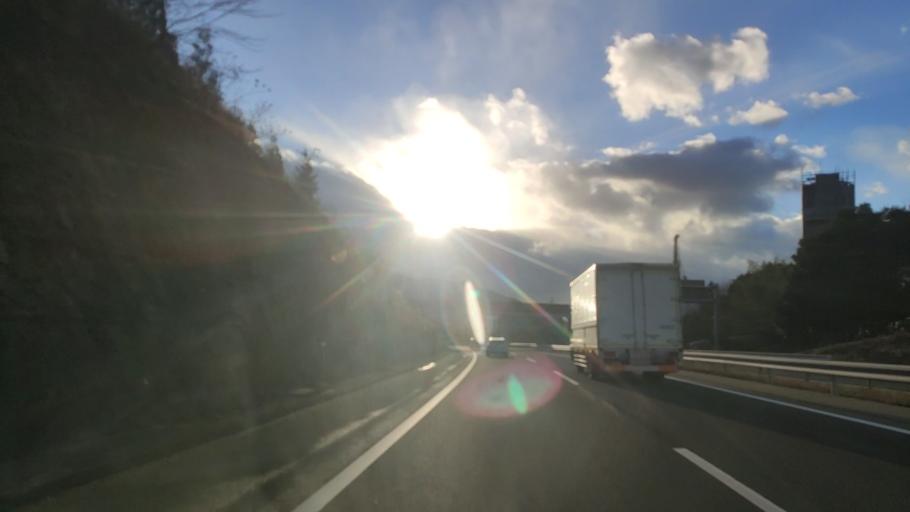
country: JP
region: Ehime
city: Saijo
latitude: 33.8705
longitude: 133.0620
